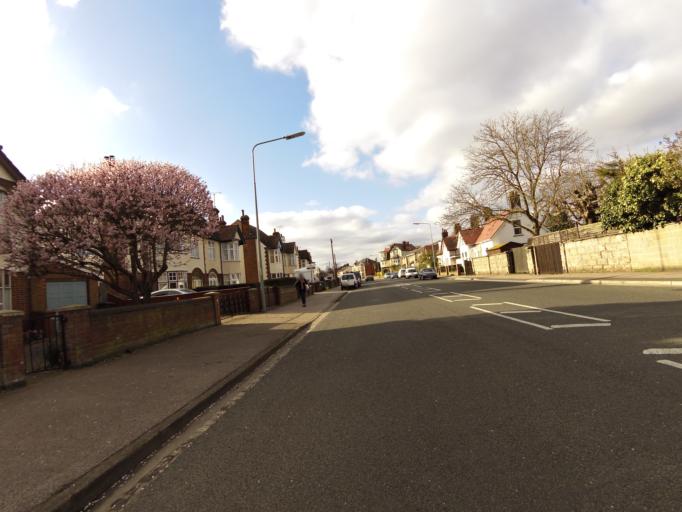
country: GB
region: England
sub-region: Suffolk
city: Ipswich
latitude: 52.0431
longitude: 1.1826
